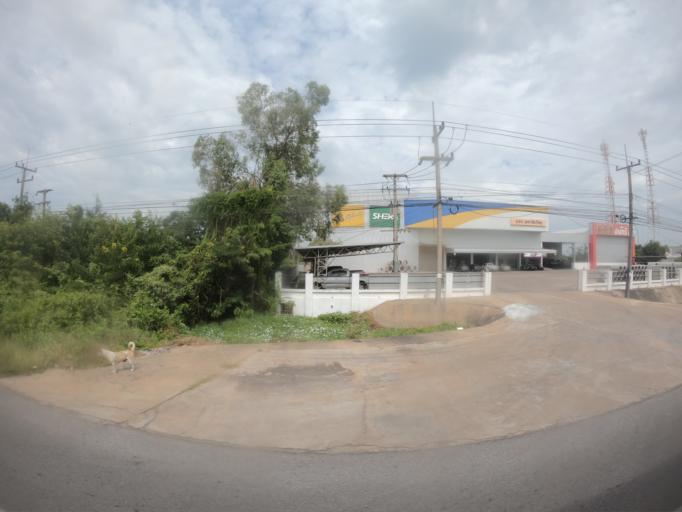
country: TH
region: Maha Sarakham
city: Maha Sarakham
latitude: 16.1608
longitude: 103.3535
